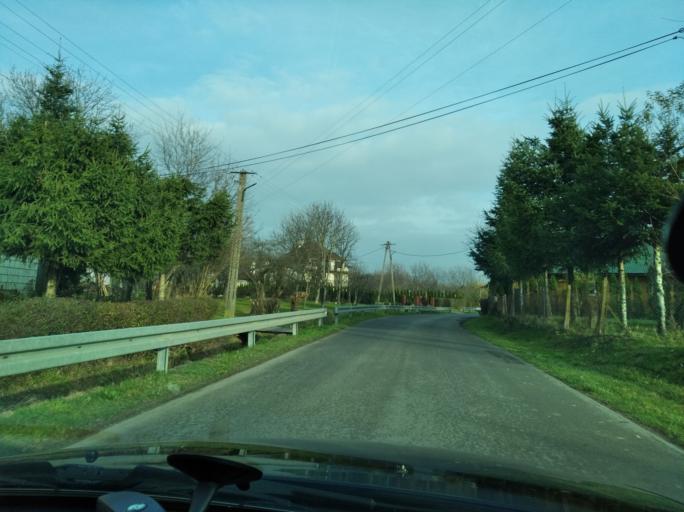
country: PL
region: Subcarpathian Voivodeship
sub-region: Powiat przeworski
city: Siedleczka
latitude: 49.9598
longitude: 22.3824
